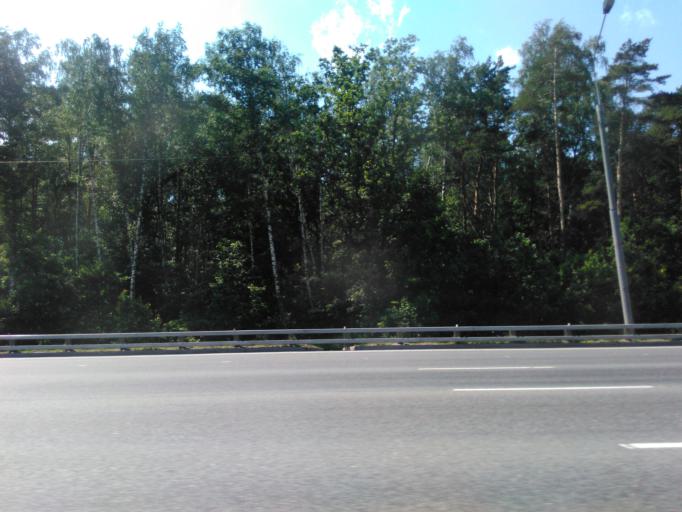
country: RU
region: Moskovskaya
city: Kotel'niki
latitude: 55.6614
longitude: 37.8396
